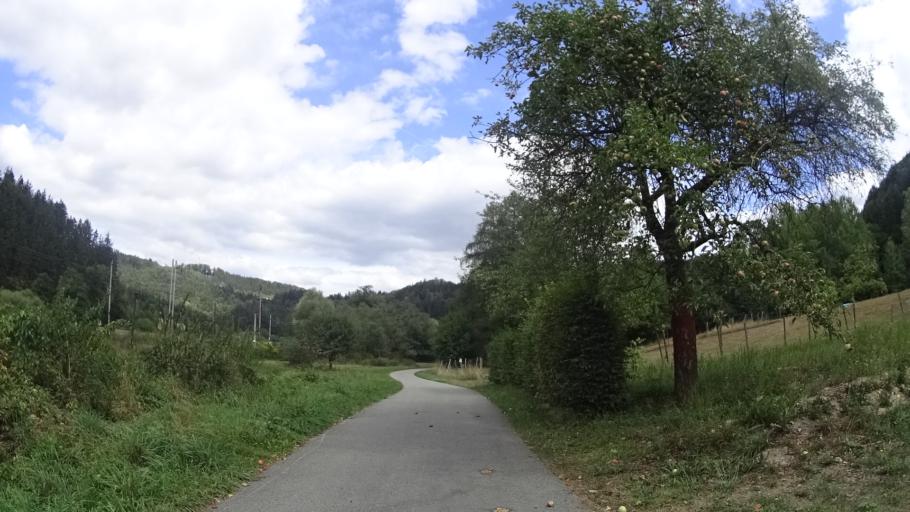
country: CZ
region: Pardubicky
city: Brandys nad Orlici
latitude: 49.9912
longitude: 16.3361
